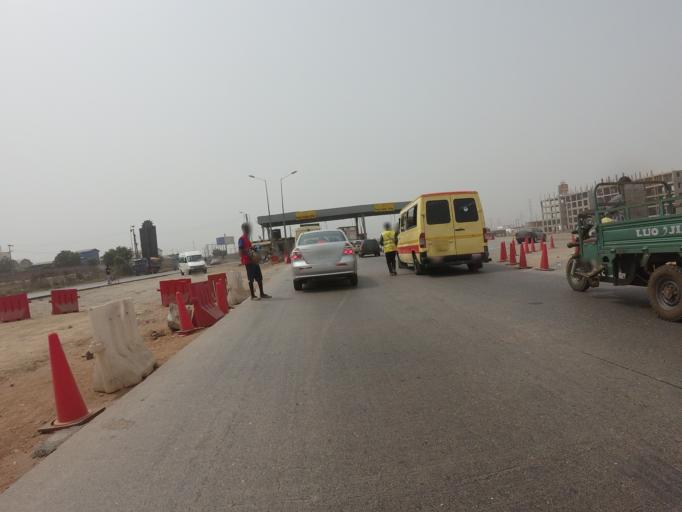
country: GH
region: Greater Accra
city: Tema
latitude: 5.6838
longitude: -0.0223
